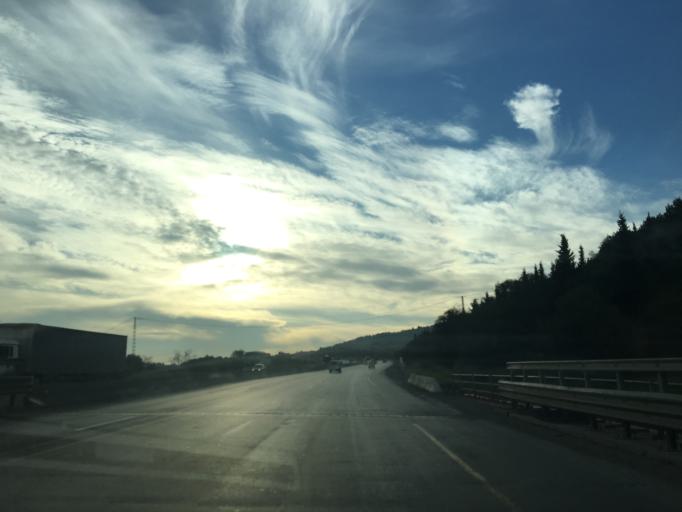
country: DZ
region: Bouira
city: Draa el Mizan
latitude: 36.4559
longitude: 3.7792
